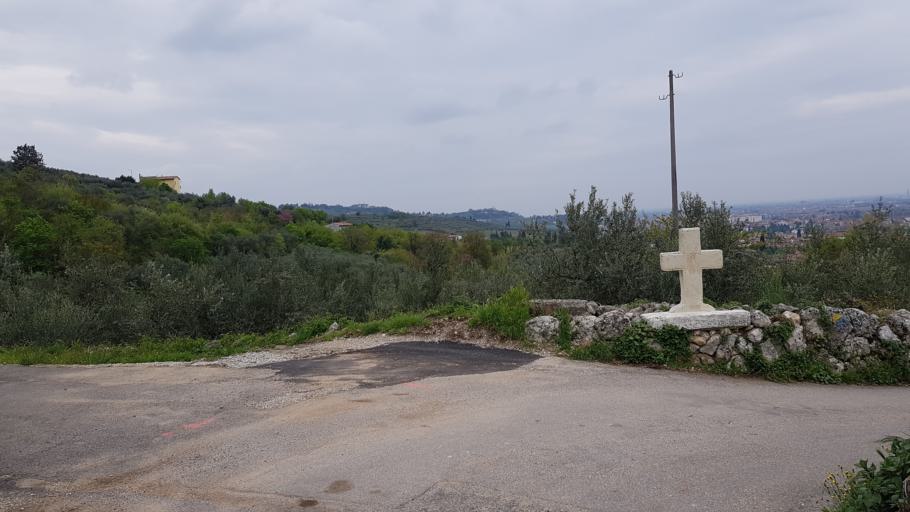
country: IT
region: Veneto
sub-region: Provincia di Verona
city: Parona
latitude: 45.4773
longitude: 10.9712
